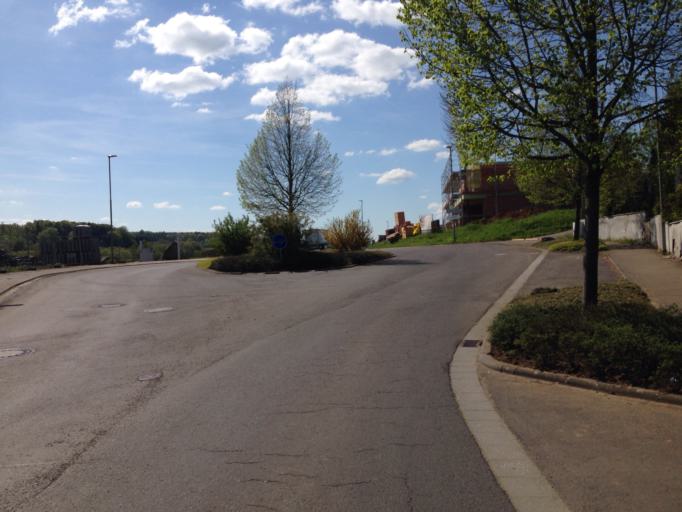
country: DE
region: Hesse
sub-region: Regierungsbezirk Giessen
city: Laubach
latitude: 50.5433
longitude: 8.9697
